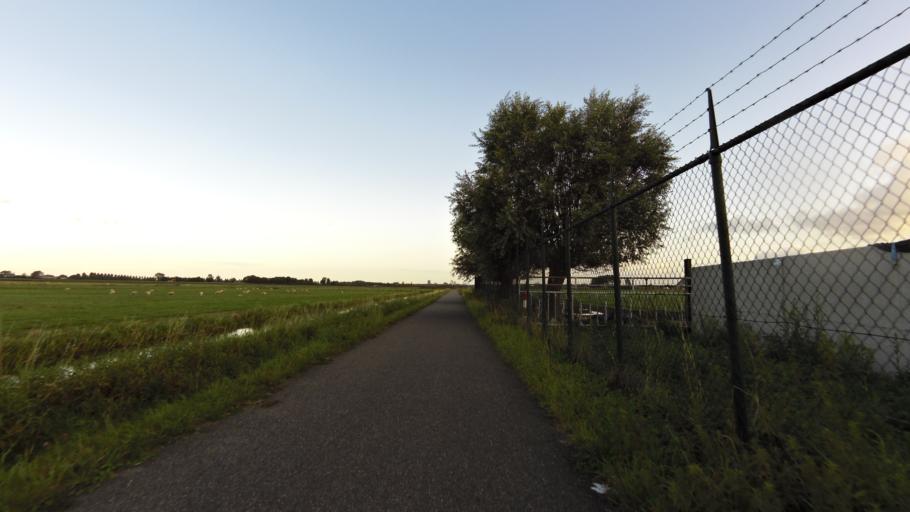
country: NL
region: South Holland
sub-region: Gemeente Voorschoten
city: Voorschoten
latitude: 52.0940
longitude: 4.4501
